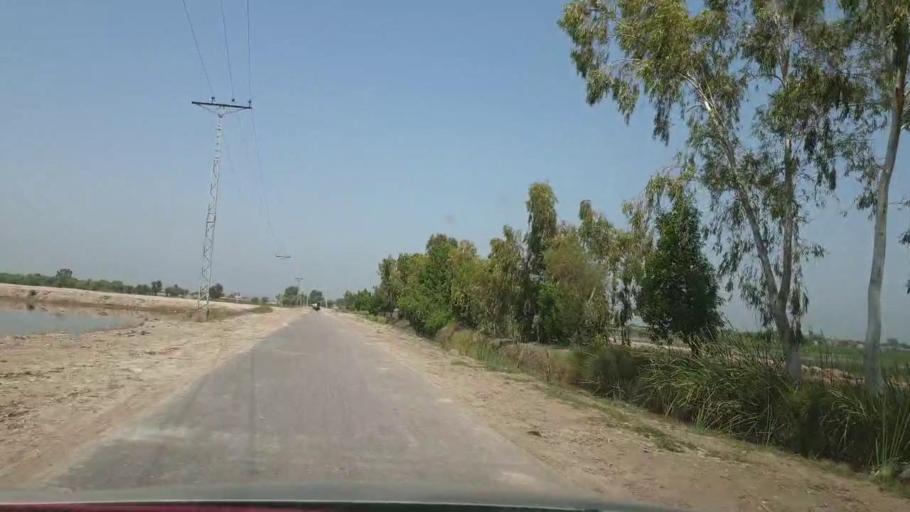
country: PK
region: Sindh
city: Warah
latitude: 27.4762
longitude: 67.7580
